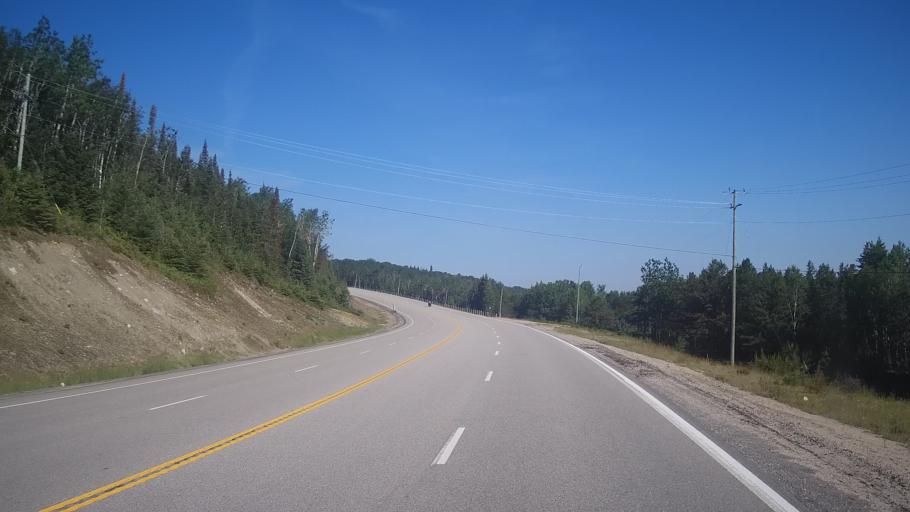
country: CA
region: Ontario
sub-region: Rainy River District
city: Atikokan
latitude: 49.4828
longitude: -91.9560
